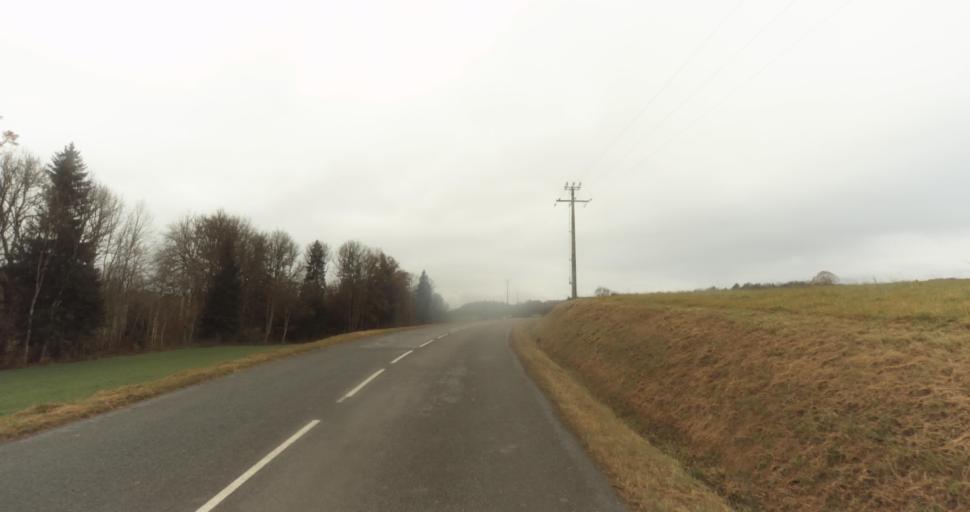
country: FR
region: Rhone-Alpes
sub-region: Departement de la Haute-Savoie
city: Evires
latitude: 46.0467
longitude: 6.2239
